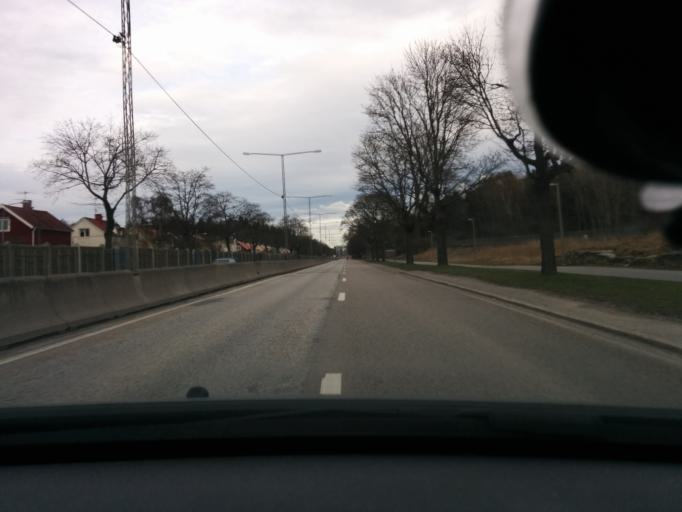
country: SE
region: Stockholm
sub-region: Stockholms Kommun
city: Bromma
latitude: 59.3421
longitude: 17.9119
